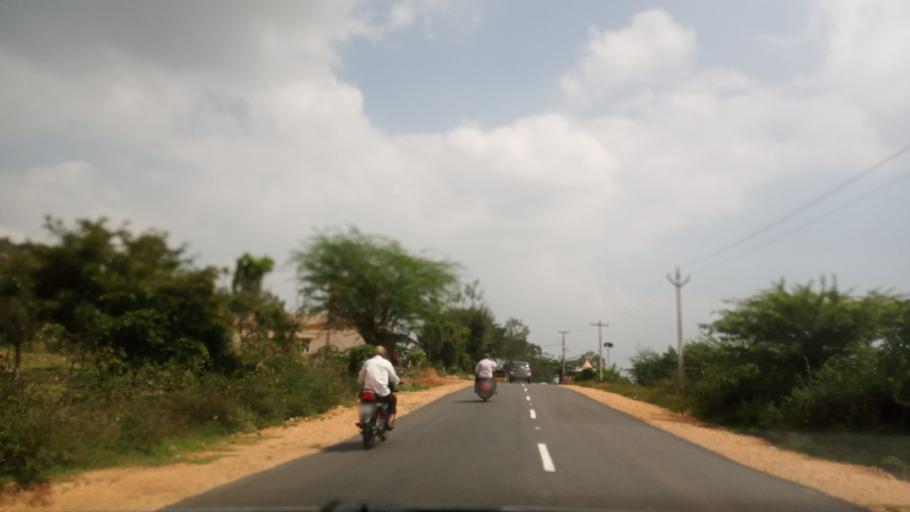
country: IN
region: Andhra Pradesh
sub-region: Chittoor
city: Madanapalle
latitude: 13.6365
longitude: 78.5960
